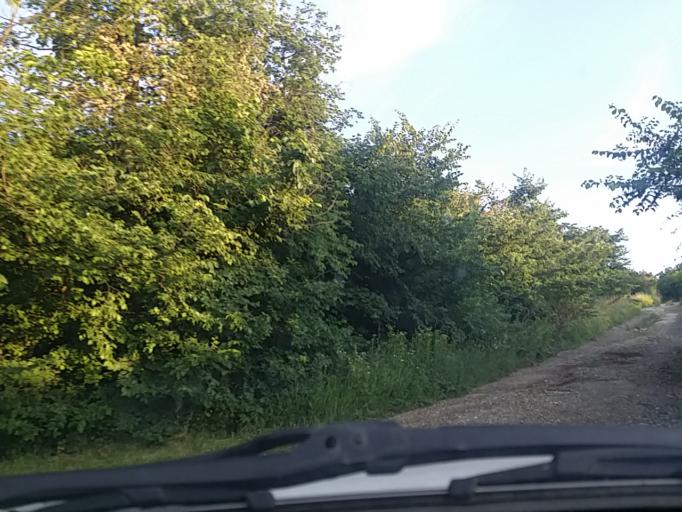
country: HU
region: Pest
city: Urom
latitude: 47.5783
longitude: 19.0258
